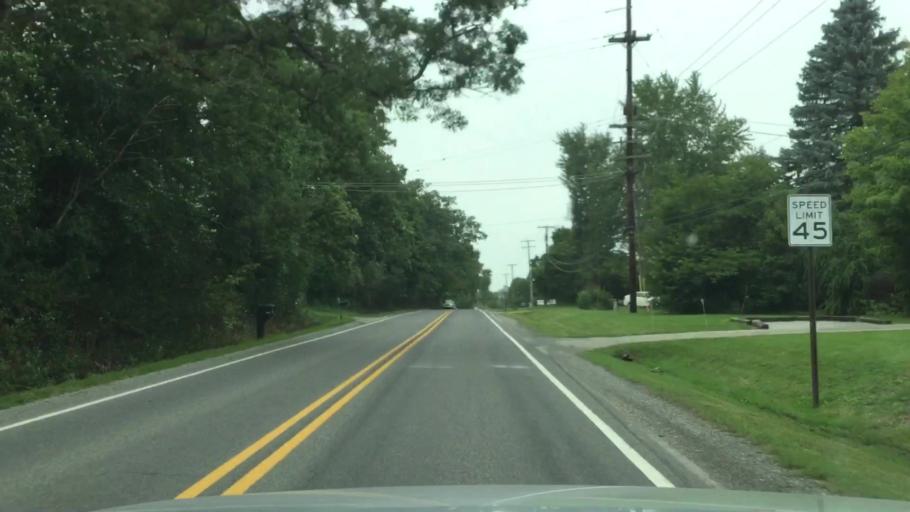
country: US
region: Michigan
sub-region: Washtenaw County
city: Ypsilanti
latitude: 42.2013
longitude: -83.6707
